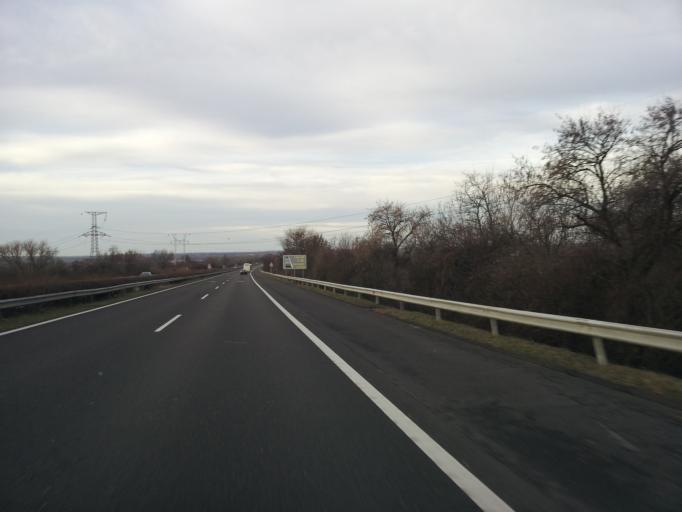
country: HU
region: Fejer
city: Lepseny
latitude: 47.0142
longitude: 18.2431
